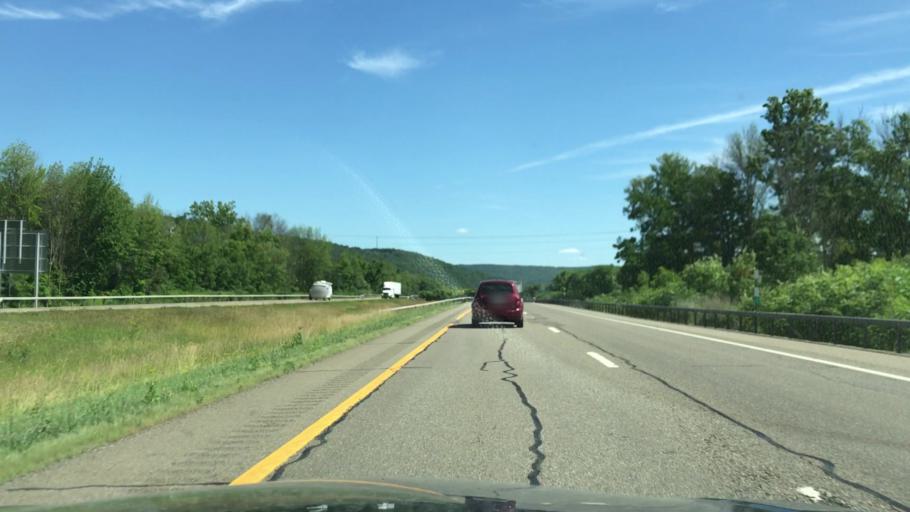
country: US
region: New York
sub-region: Steuben County
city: Gang Mills
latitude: 42.2136
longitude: -77.1755
